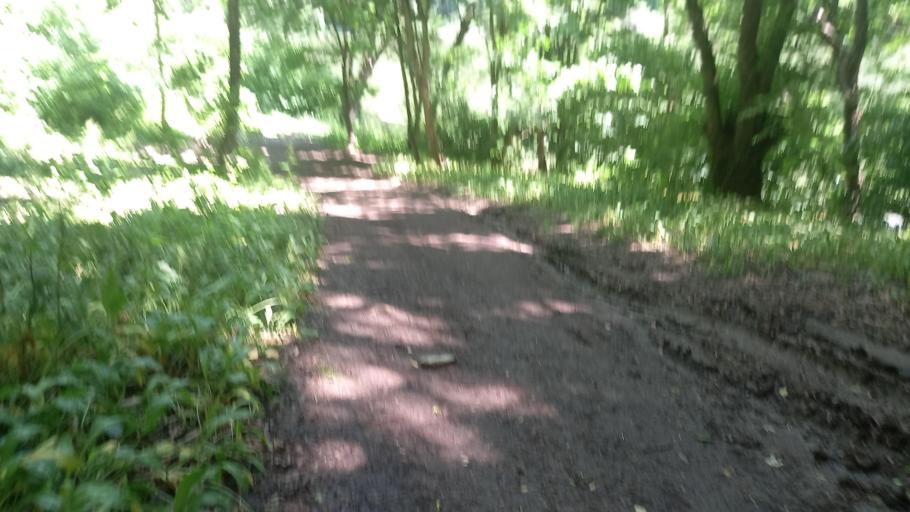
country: RU
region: Karachayevo-Cherkesiya
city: Pregradnaya
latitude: 44.1038
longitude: 41.1386
